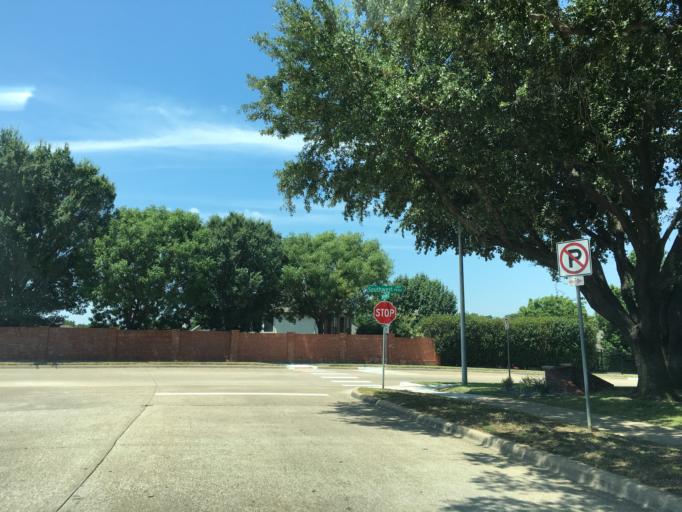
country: US
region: Texas
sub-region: Denton County
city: Lewisville
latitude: 33.0222
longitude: -96.9988
